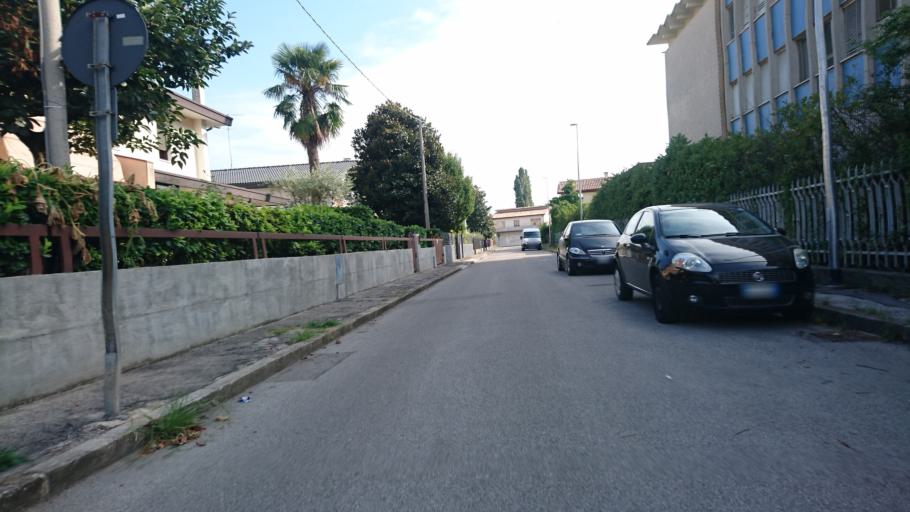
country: IT
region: Veneto
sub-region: Provincia di Padova
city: Tencarola
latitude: 45.3938
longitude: 11.8063
